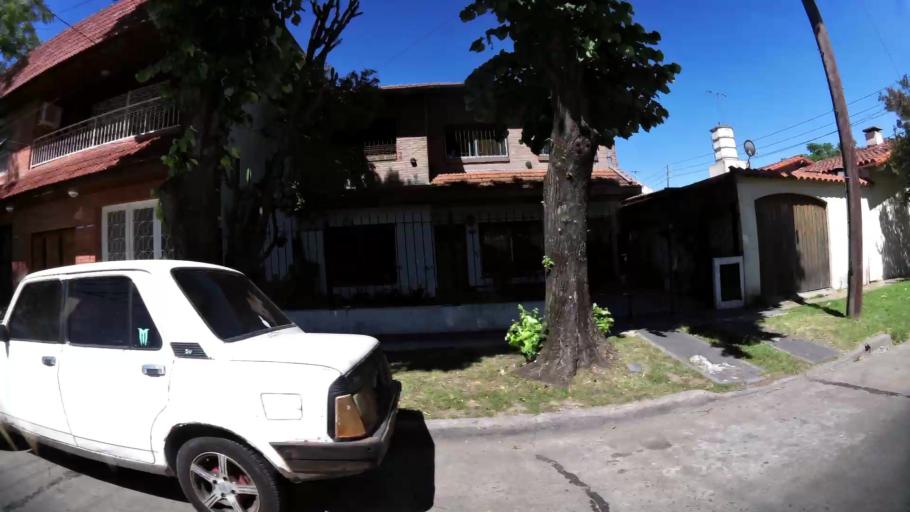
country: AR
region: Buenos Aires
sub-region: Partido de General San Martin
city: General San Martin
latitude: -34.5232
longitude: -58.5338
